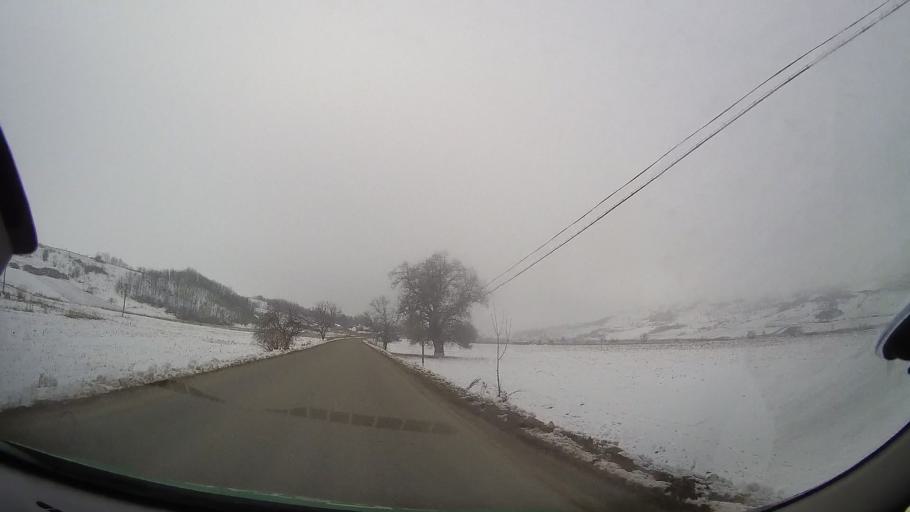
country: RO
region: Bacau
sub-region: Comuna Glavanesti
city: Frumuselu
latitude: 46.2933
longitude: 27.3008
